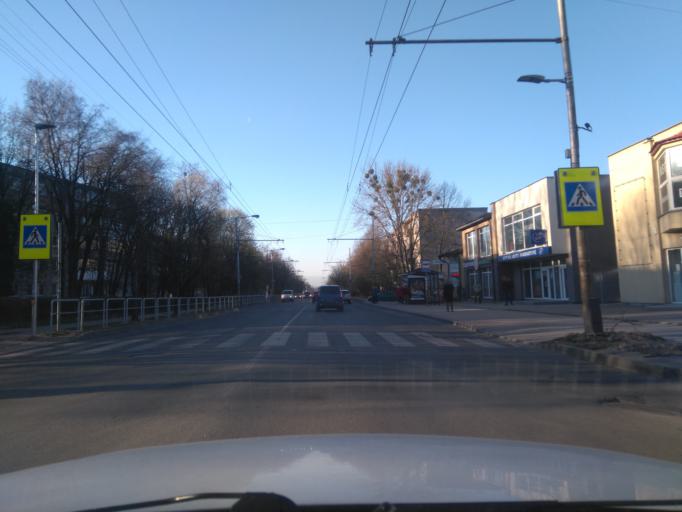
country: LT
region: Kauno apskritis
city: Dainava (Kaunas)
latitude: 54.9102
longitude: 23.9738
